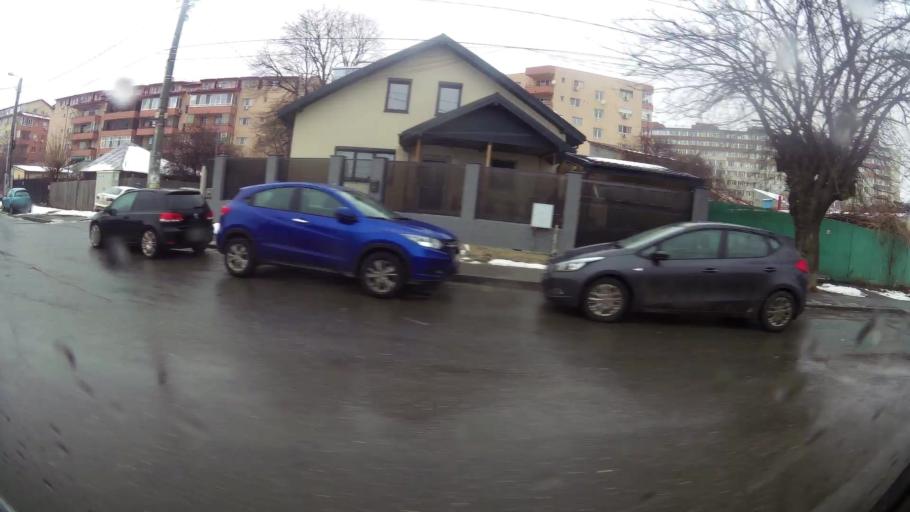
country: RO
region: Ilfov
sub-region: Comuna Chiajna
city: Rosu
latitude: 44.4115
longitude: 26.0217
